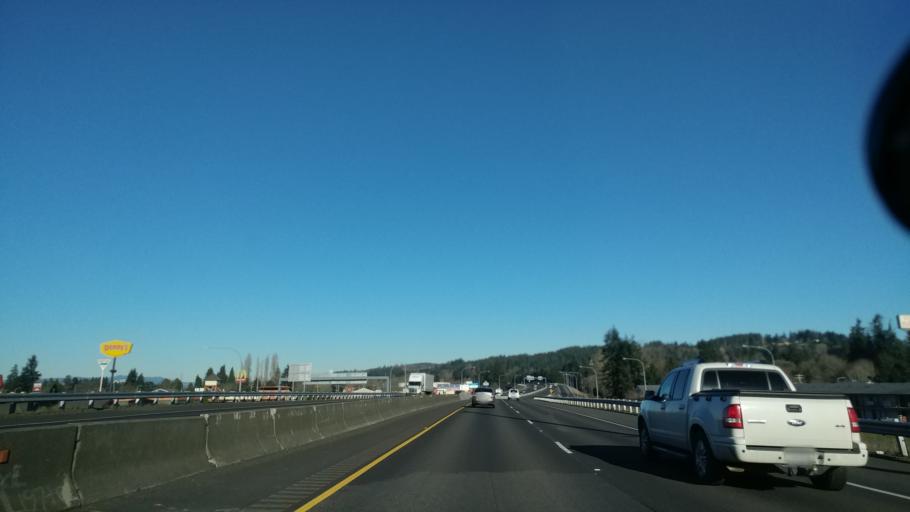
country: US
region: Washington
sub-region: Lewis County
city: Fords Prairie
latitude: 46.7270
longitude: -122.9771
